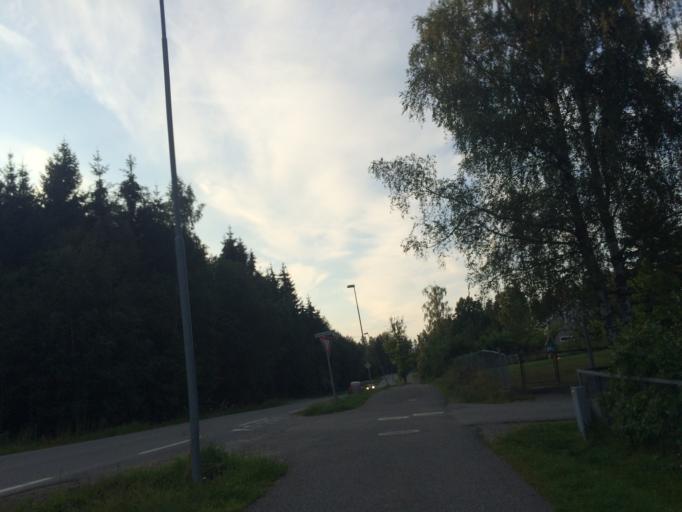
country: NO
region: Akershus
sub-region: Ski
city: Ski
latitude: 59.6997
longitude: 10.8463
